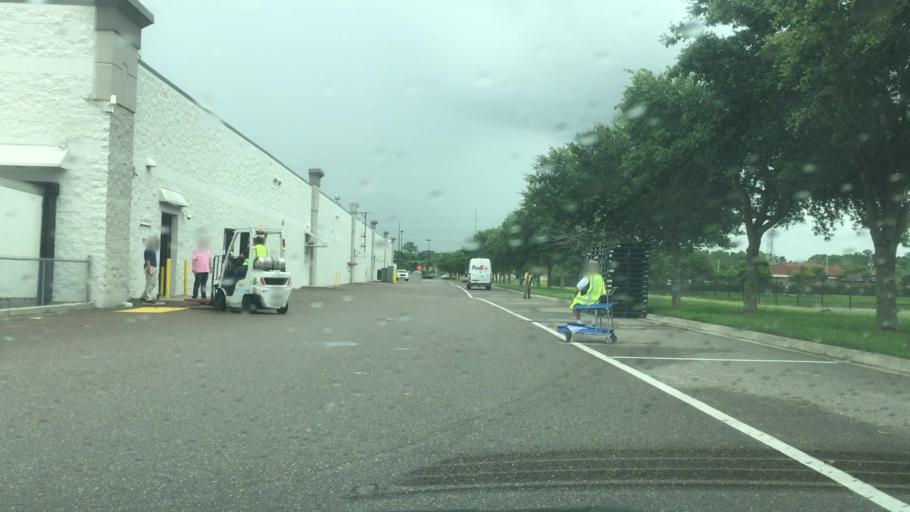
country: US
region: Florida
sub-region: Duval County
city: Atlantic Beach
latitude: 30.3165
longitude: -81.4928
